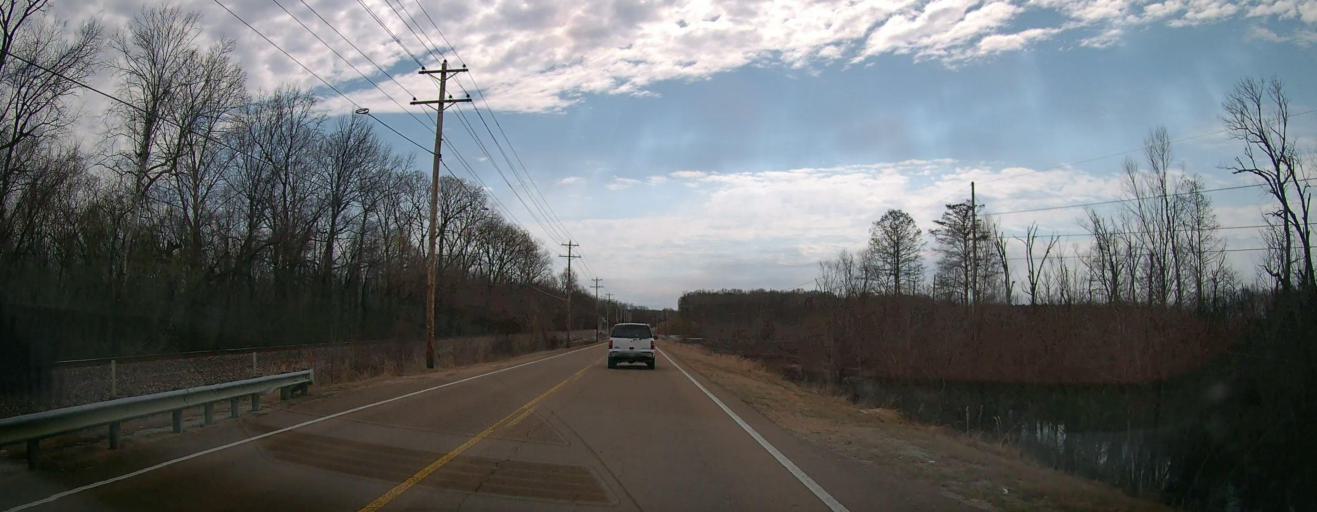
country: US
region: Mississippi
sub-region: Marshall County
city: Byhalia
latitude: 34.9061
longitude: -89.7512
